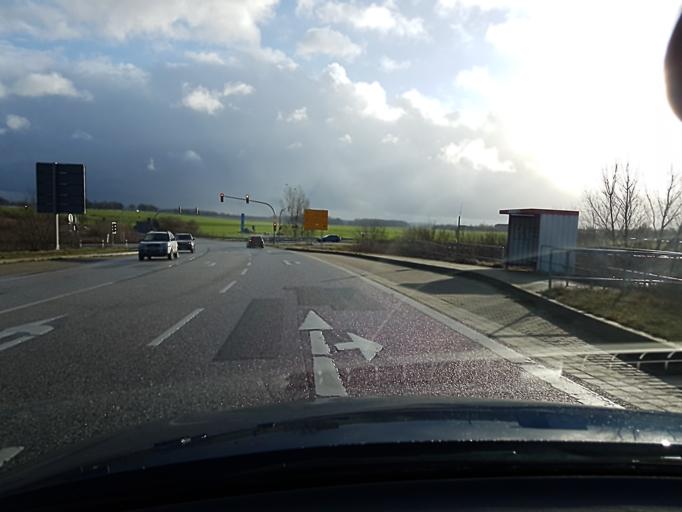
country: DE
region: Mecklenburg-Vorpommern
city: Dummerstorf
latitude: 54.0242
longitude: 12.2328
